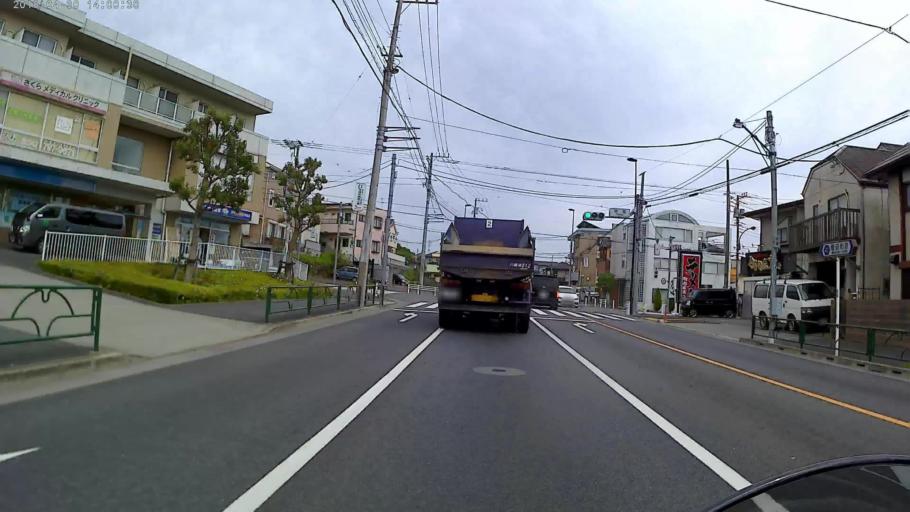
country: JP
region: Tokyo
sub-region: Machida-shi
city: Machida
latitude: 35.5860
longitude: 139.3946
